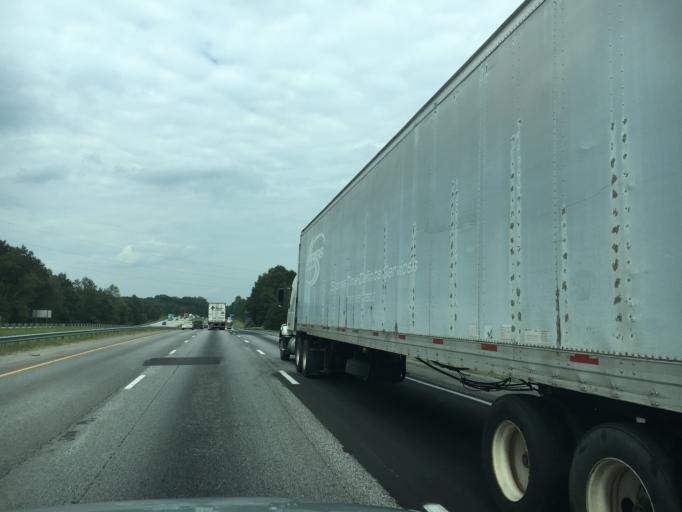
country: US
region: South Carolina
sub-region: Anderson County
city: Northlake
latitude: 34.6237
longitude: -82.6142
